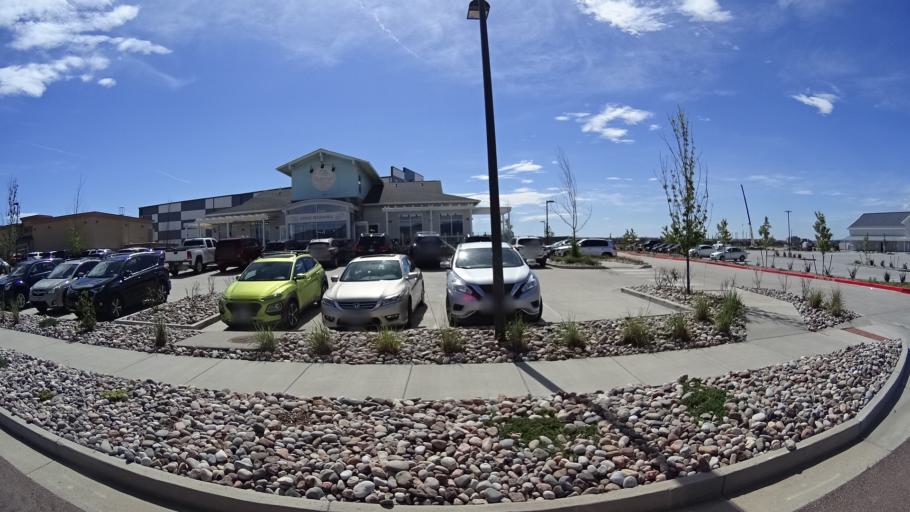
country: US
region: Colorado
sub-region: El Paso County
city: Gleneagle
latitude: 39.0241
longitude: -104.8243
